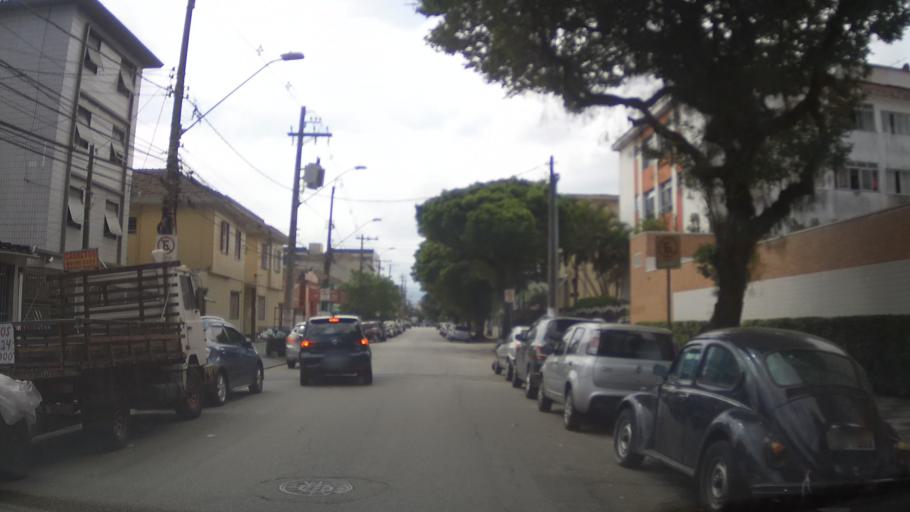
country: BR
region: Sao Paulo
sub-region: Santos
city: Santos
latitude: -23.9600
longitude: -46.3163
